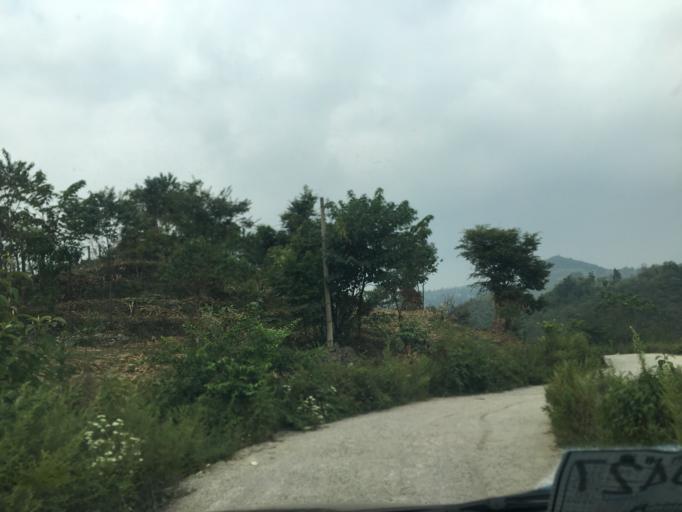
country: CN
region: Guangxi Zhuangzu Zizhiqu
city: Xinzhou
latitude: 25.5687
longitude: 105.6158
